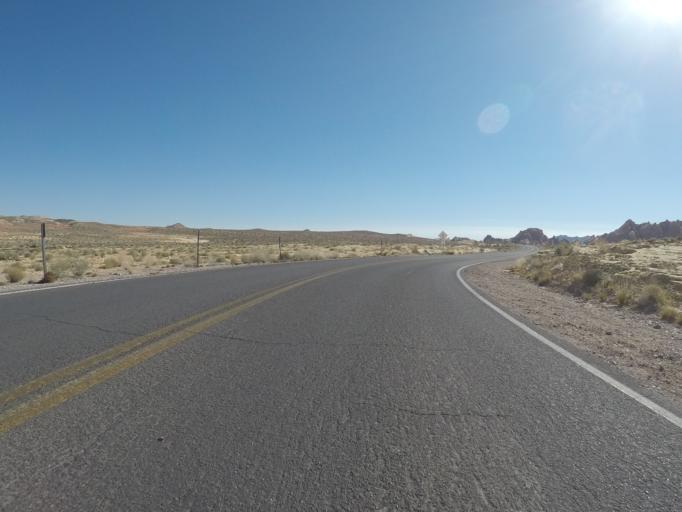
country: US
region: Nevada
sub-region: Clark County
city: Moapa Valley
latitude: 36.4647
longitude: -114.5227
